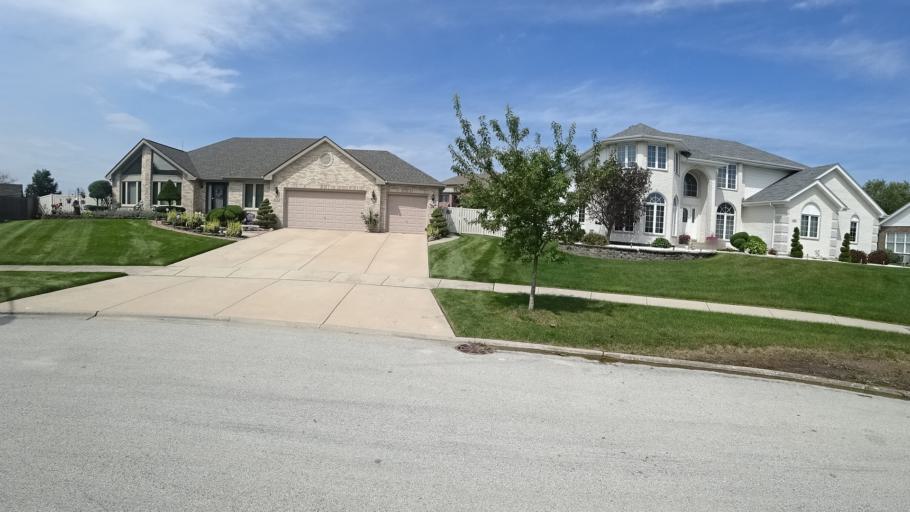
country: US
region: Illinois
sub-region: Cook County
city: Orland Hills
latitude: 41.5548
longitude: -87.8360
